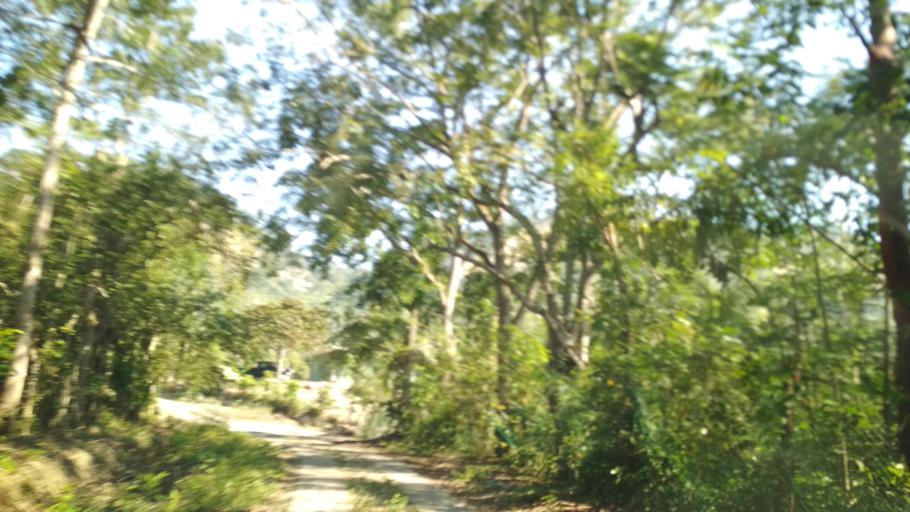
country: MX
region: Veracruz
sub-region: Papantla
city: Polutla
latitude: 20.4633
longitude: -97.1926
